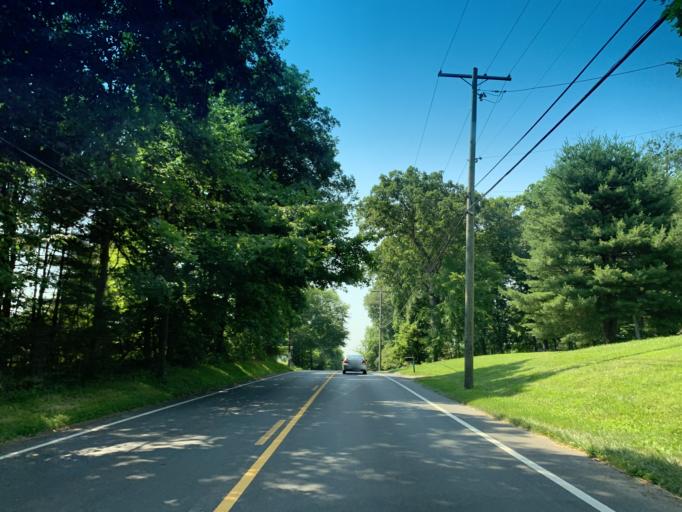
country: US
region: Maryland
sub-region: Montgomery County
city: Darnestown
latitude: 39.1250
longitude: -77.3273
